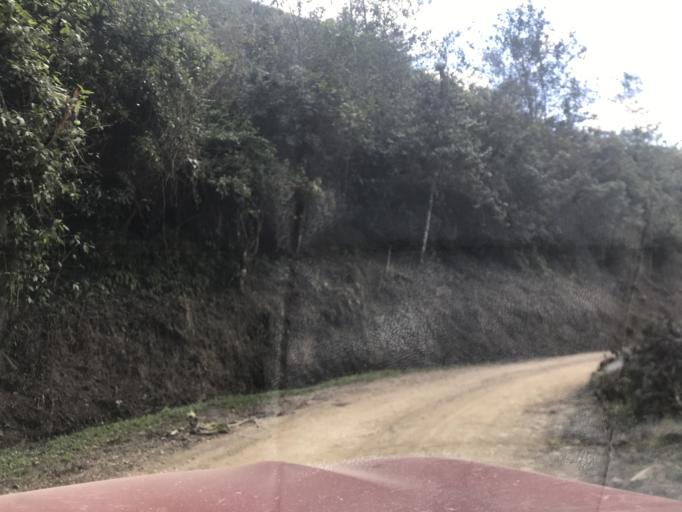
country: PE
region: Cajamarca
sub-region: Provincia de Chota
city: Querocoto
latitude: -6.3459
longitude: -79.0507
